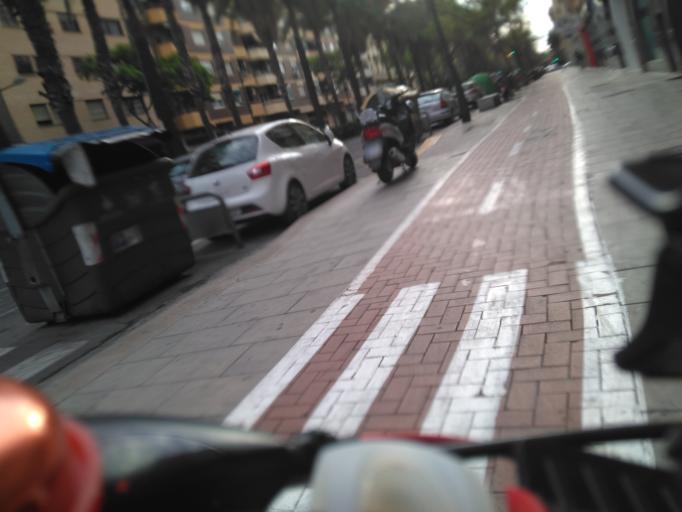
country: ES
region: Valencia
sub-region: Provincia de Valencia
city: Valencia
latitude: 39.4855
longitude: -0.3785
